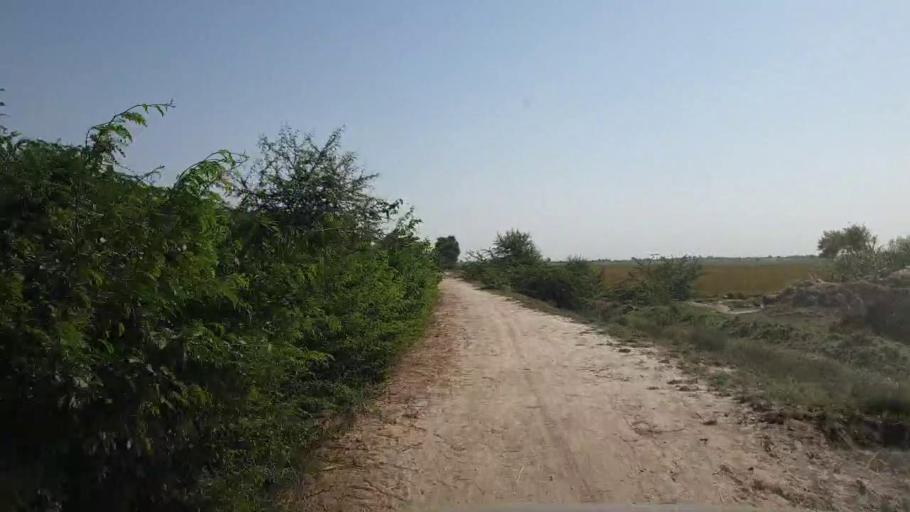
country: PK
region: Sindh
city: Kadhan
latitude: 24.6107
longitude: 68.9995
